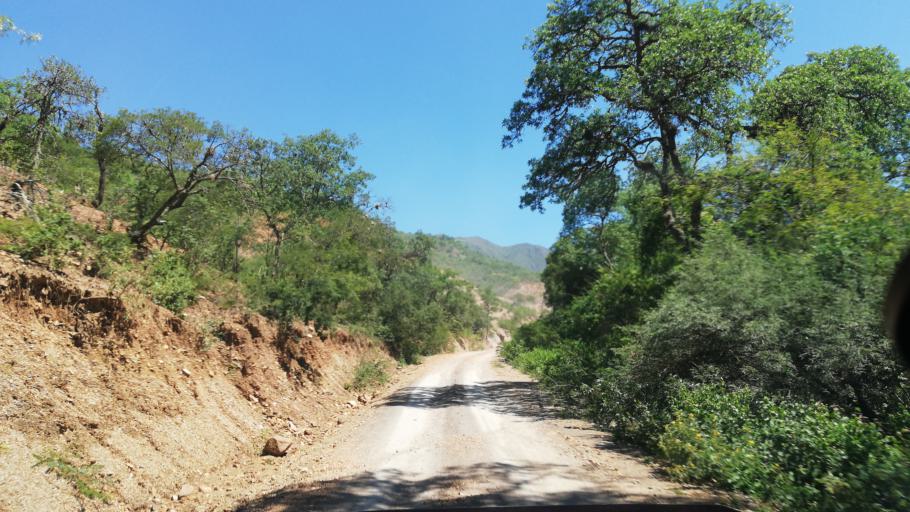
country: BO
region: Cochabamba
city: Mizque
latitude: -17.8873
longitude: -65.2836
